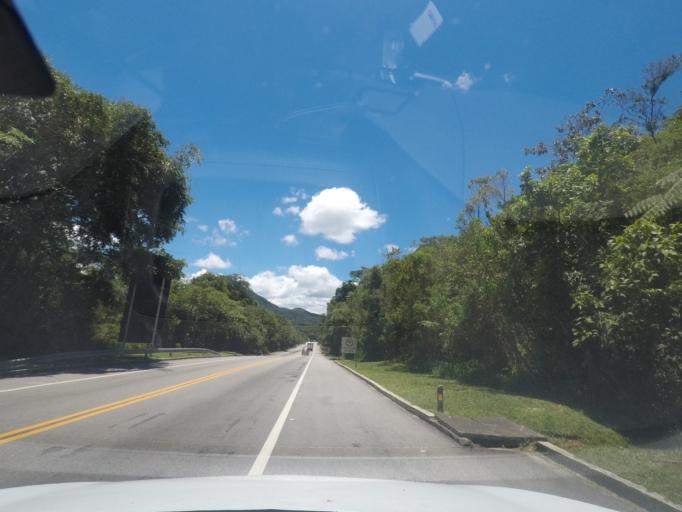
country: BR
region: Rio de Janeiro
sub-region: Teresopolis
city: Teresopolis
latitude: -22.4607
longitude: -42.9810
